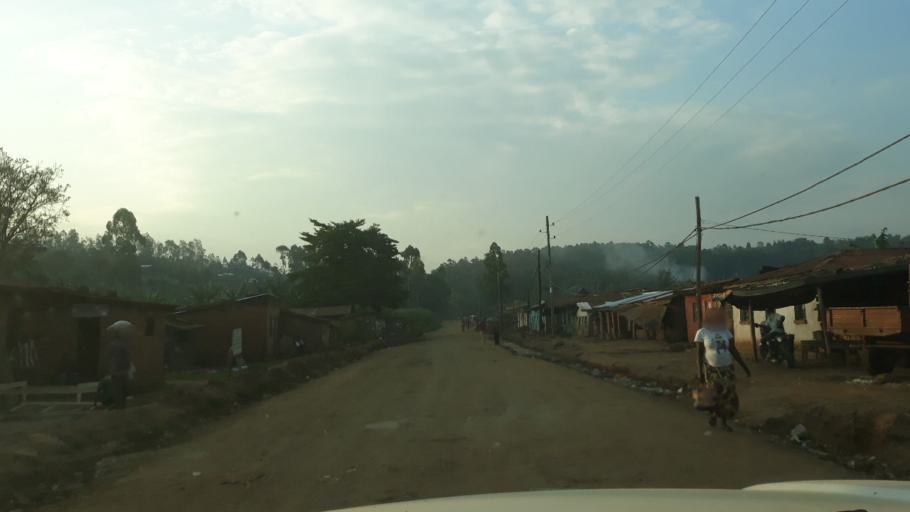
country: CD
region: South Kivu
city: Bukavu
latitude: -2.6588
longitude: 28.8740
